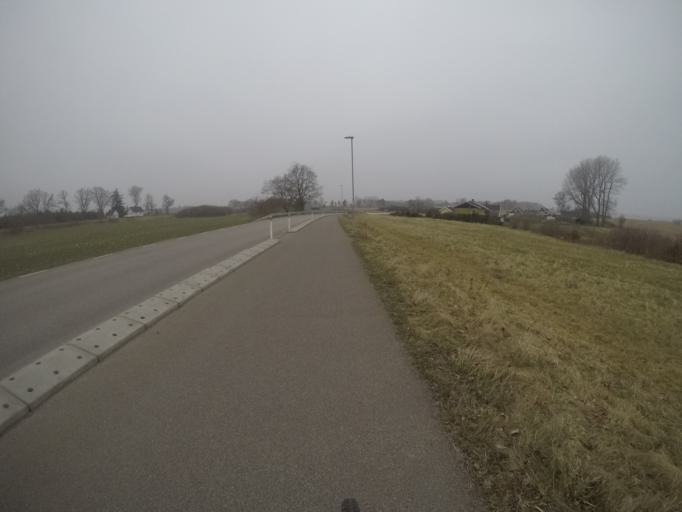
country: SE
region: Skane
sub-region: Angelholms Kommun
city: Strovelstorp
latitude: 56.2166
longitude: 12.7721
